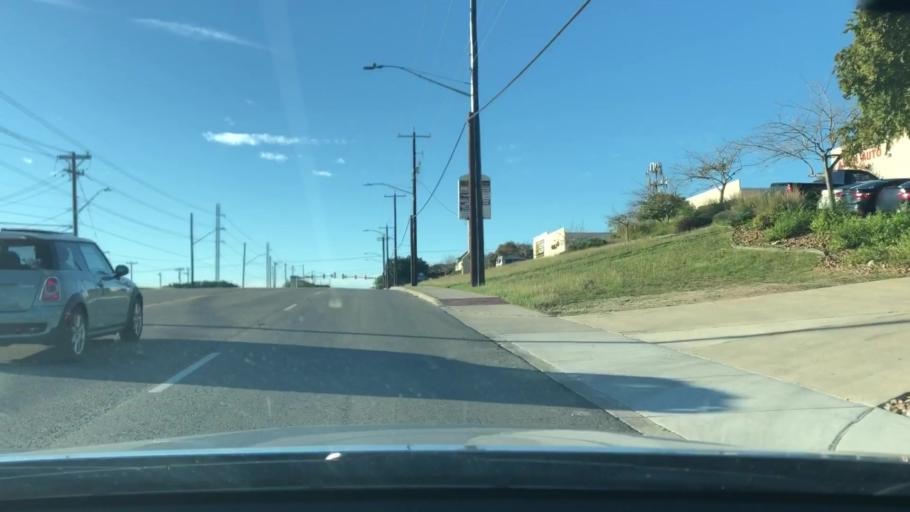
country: US
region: Texas
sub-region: Bexar County
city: Hollywood Park
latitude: 29.5512
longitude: -98.4658
